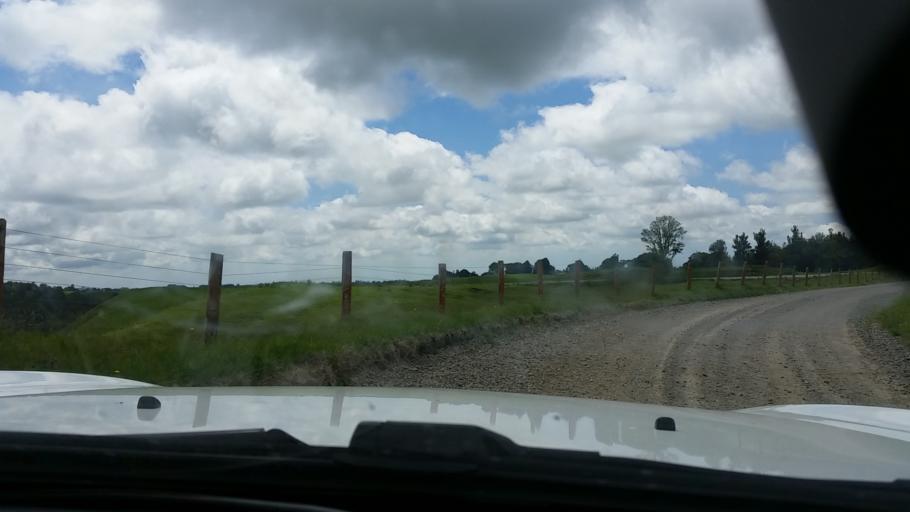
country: NZ
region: Bay of Plenty
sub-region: Western Bay of Plenty District
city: Maketu
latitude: -37.9702
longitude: 176.4350
